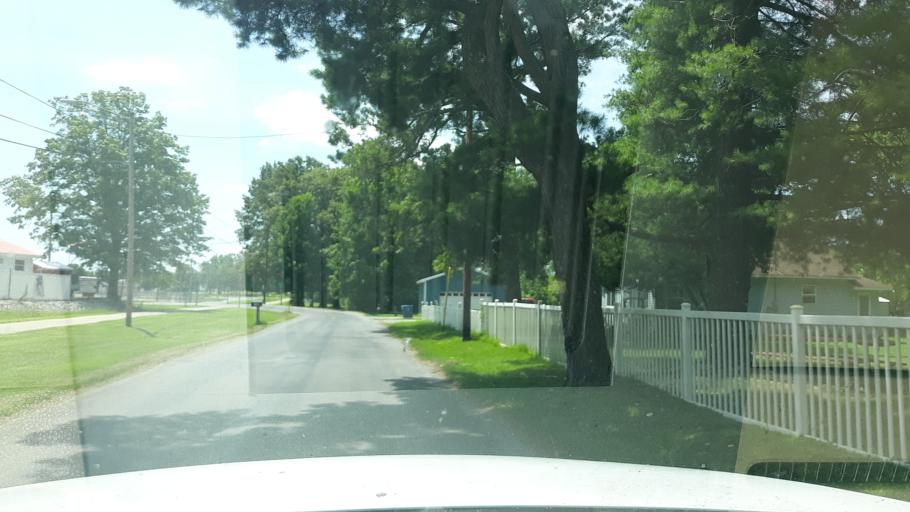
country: US
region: Illinois
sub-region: Saline County
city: Eldorado
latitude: 37.8056
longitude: -88.4331
